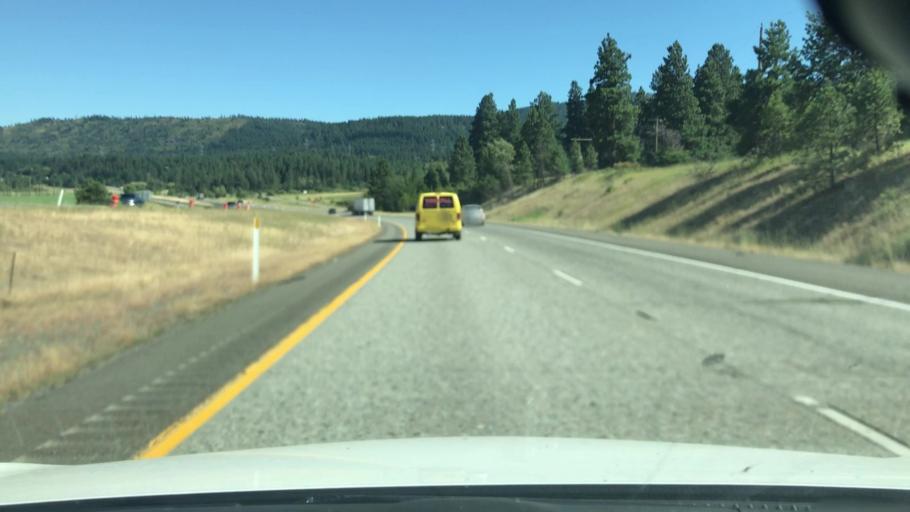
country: US
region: Washington
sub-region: Kittitas County
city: Cle Elum
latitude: 47.1735
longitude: -120.8896
